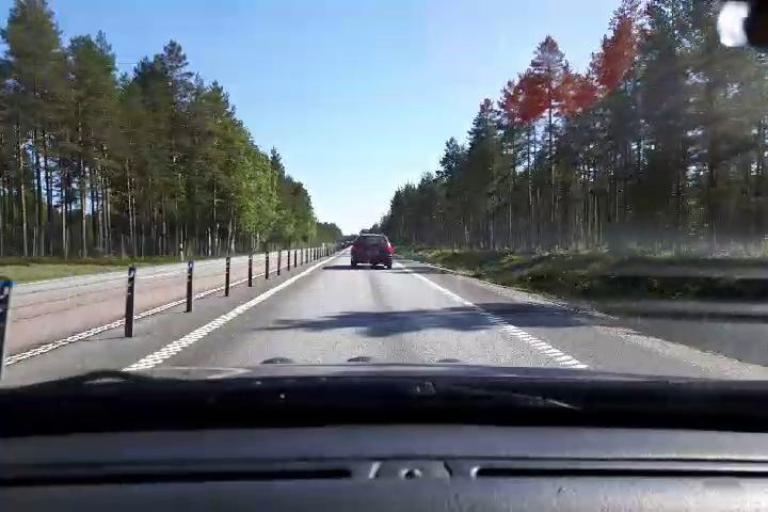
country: SE
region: Gaevleborg
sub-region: Gavle Kommun
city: Norrsundet
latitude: 61.0259
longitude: 16.9756
